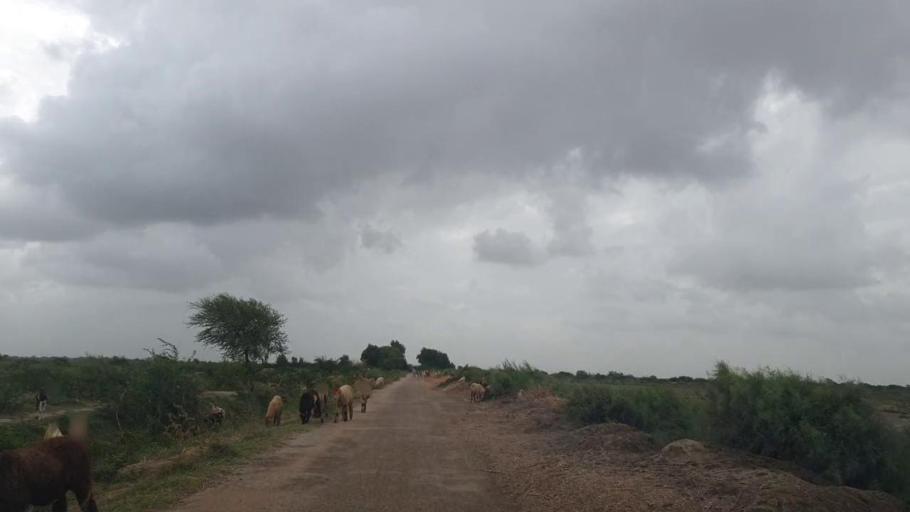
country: PK
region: Sindh
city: Tando Bago
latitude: 24.8482
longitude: 69.1608
